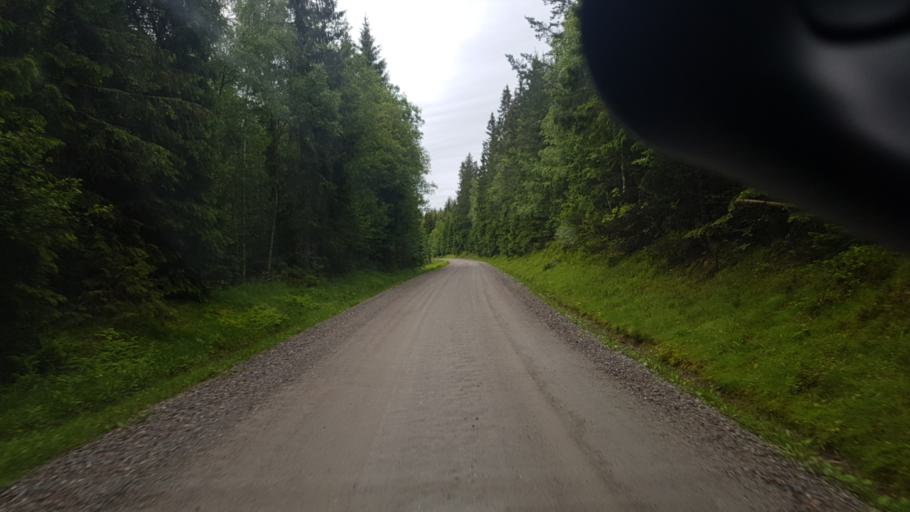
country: NO
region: Ostfold
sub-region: Romskog
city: Romskog
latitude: 59.7150
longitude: 11.9987
